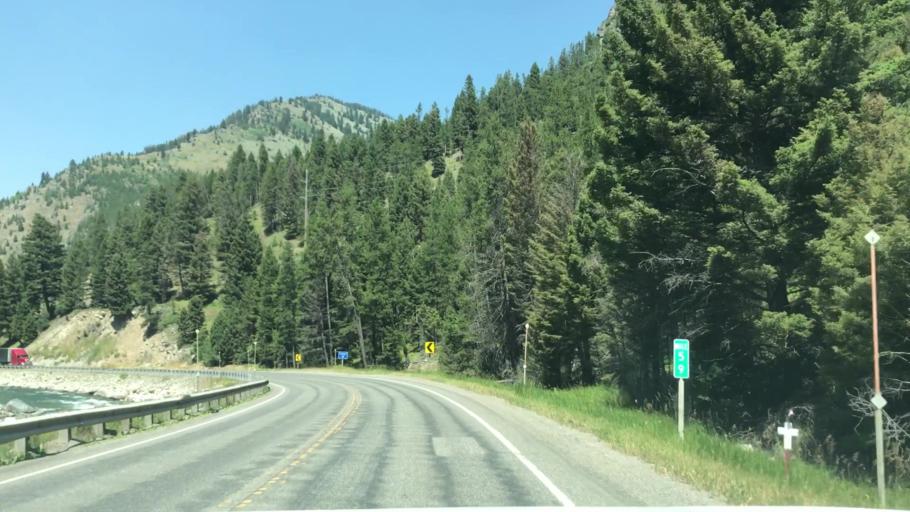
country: US
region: Montana
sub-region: Gallatin County
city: Big Sky
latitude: 45.3847
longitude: -111.1938
